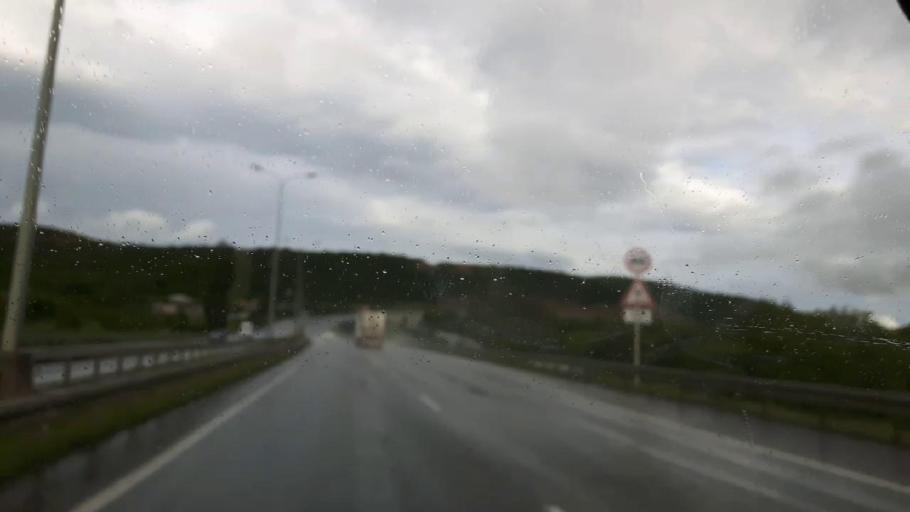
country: GE
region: Shida Kartli
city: Kaspi
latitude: 41.9940
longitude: 44.4157
